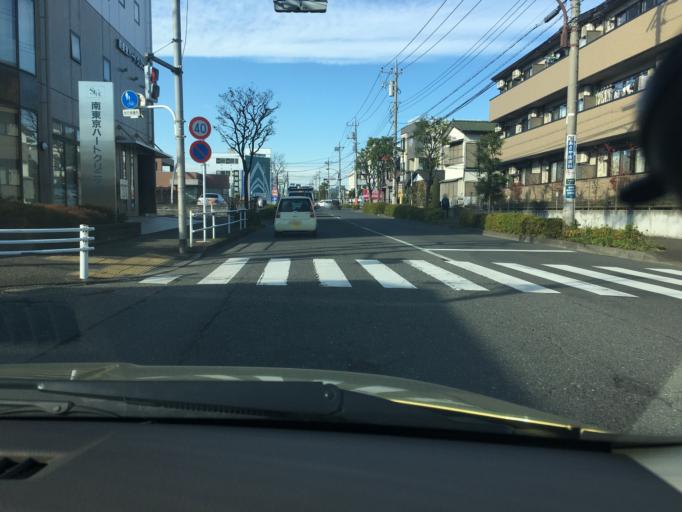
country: JP
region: Tokyo
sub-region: Machida-shi
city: Machida
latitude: 35.5686
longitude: 139.4172
